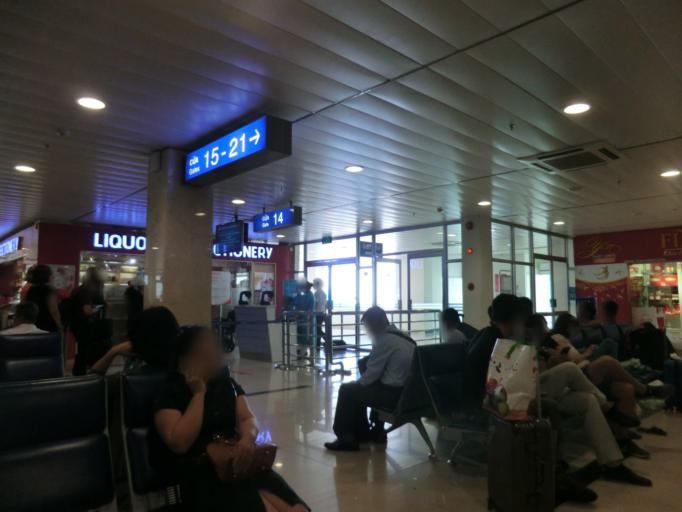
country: VN
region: Ho Chi Minh City
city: Quan Binh Thanh
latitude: 10.8261
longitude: 106.6801
